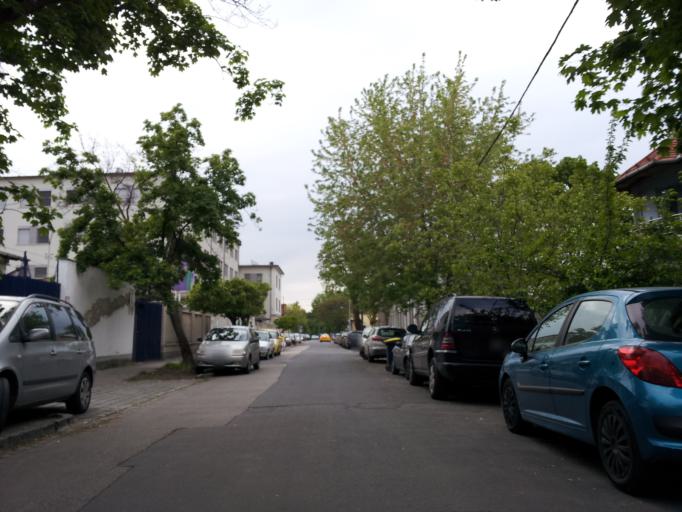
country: HU
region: Budapest
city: Budapest XIV. keruelet
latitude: 47.5258
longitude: 19.1063
